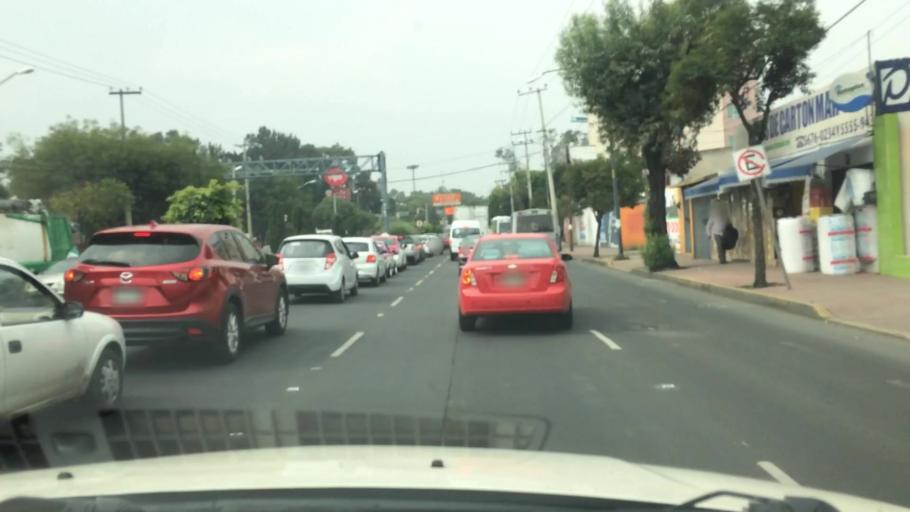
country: MX
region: Mexico City
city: Xochimilco
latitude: 19.2812
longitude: -99.1241
